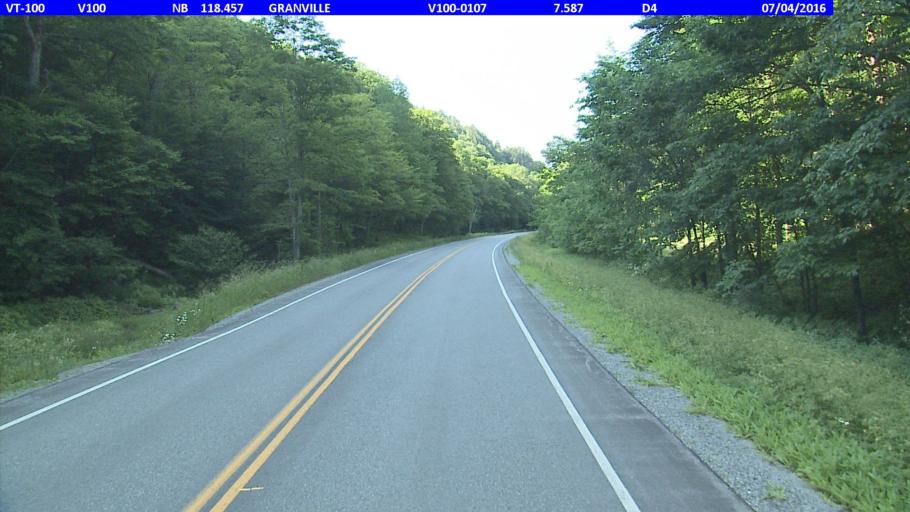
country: US
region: Vermont
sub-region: Orange County
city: Randolph
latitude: 44.0397
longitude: -72.8325
